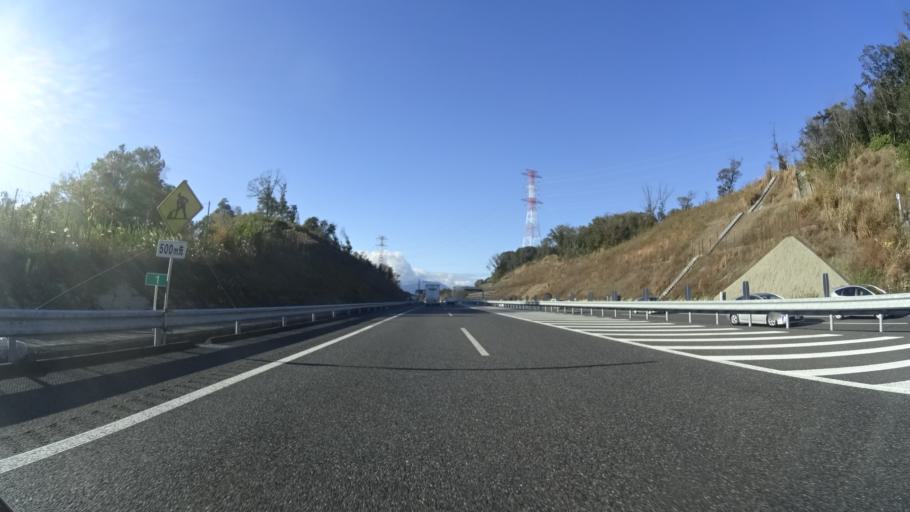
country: JP
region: Mie
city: Yokkaichi
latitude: 35.0426
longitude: 136.6203
